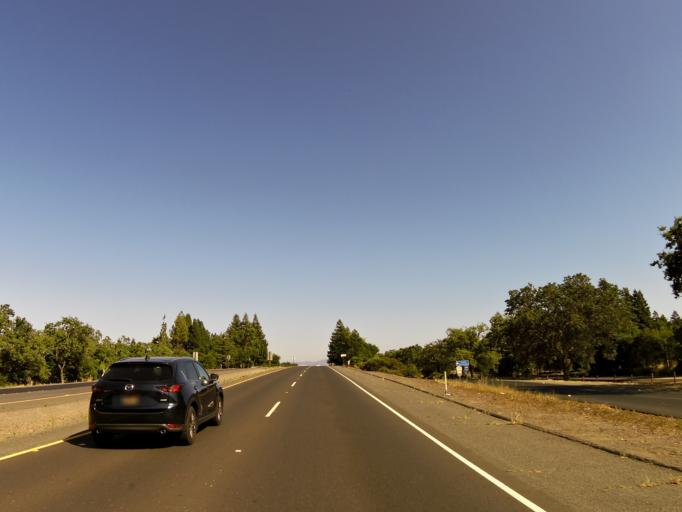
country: US
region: California
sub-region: Napa County
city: Yountville
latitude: 38.3989
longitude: -122.3606
